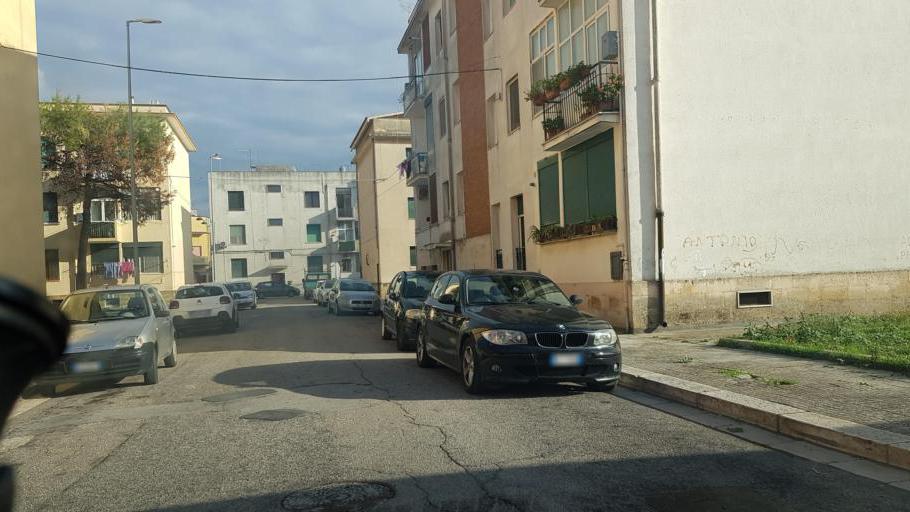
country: IT
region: Apulia
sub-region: Provincia di Brindisi
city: Francavilla Fontana
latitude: 40.5278
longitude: 17.5770
